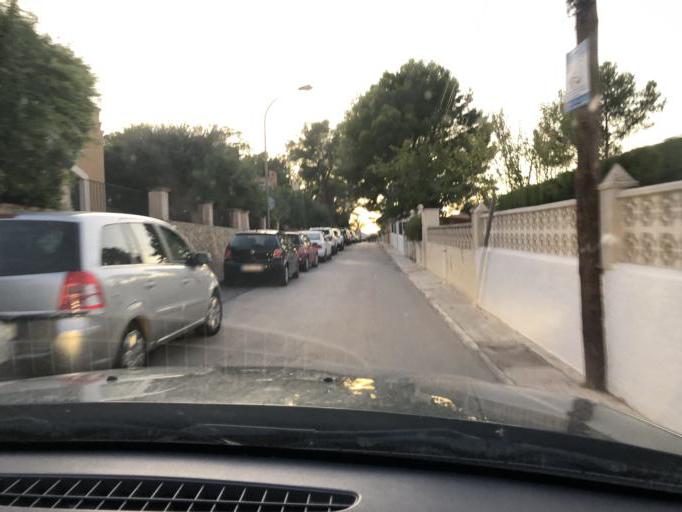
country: ES
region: Balearic Islands
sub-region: Illes Balears
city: Santa Ponsa
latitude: 39.5242
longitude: 2.4820
